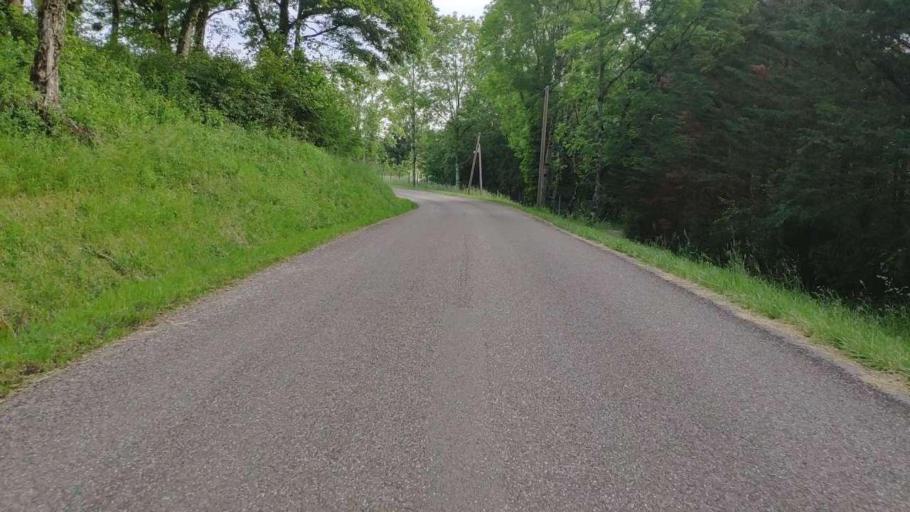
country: FR
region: Franche-Comte
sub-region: Departement du Jura
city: Perrigny
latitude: 46.7194
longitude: 5.5936
